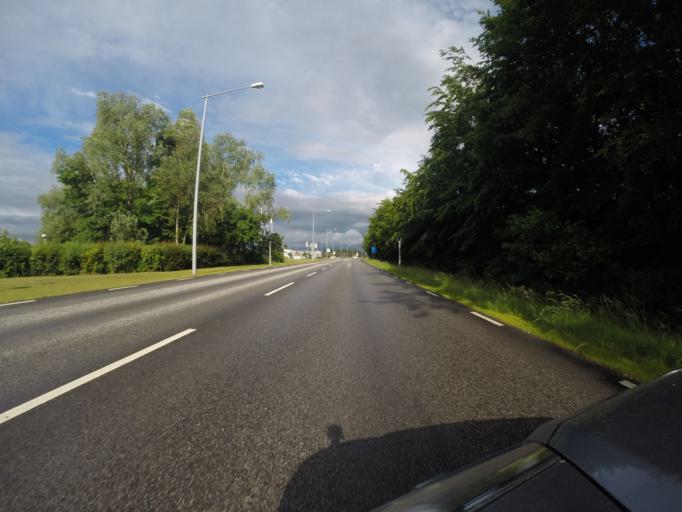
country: SE
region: Skane
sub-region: Kavlinge Kommun
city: Loddekopinge
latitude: 55.7664
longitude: 12.9954
